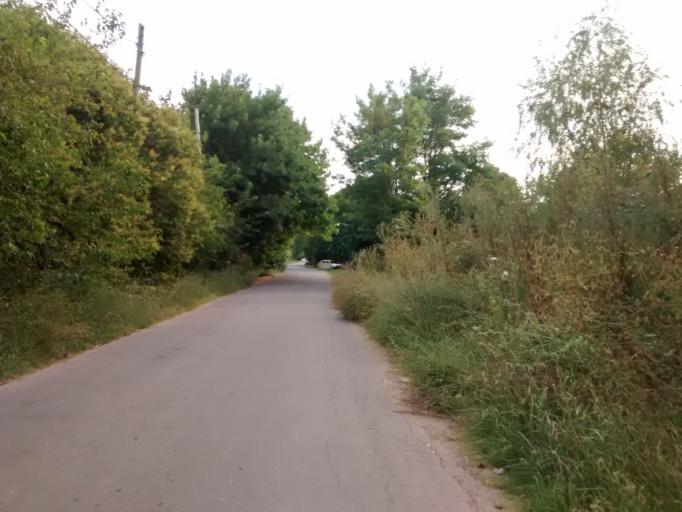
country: AR
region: Buenos Aires
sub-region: Partido de La Plata
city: La Plata
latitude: -34.8506
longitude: -58.0952
